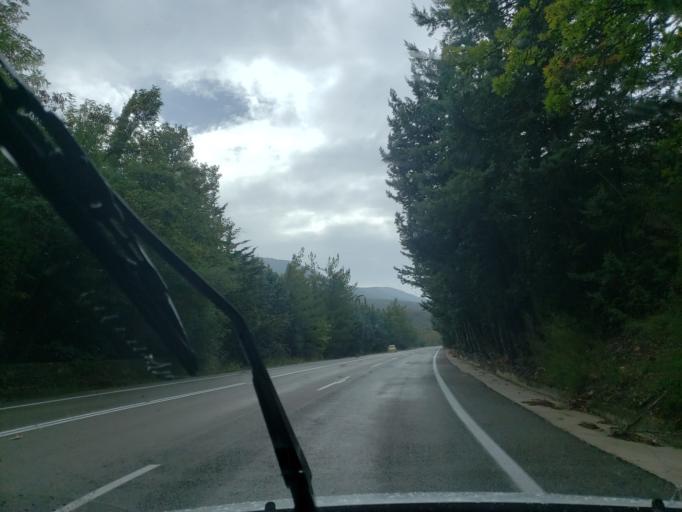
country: GR
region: Central Greece
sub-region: Nomos Fthiotidos
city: Anthili
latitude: 38.7872
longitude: 22.4934
